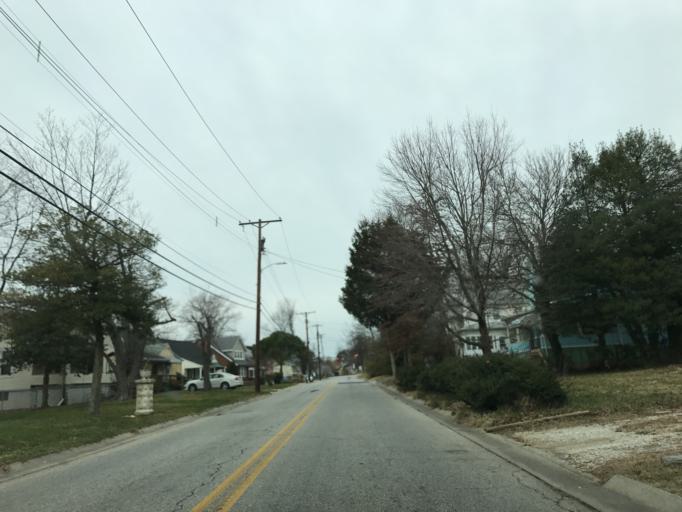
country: US
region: Maryland
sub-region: Baltimore County
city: Parkville
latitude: 39.3461
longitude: -76.5528
